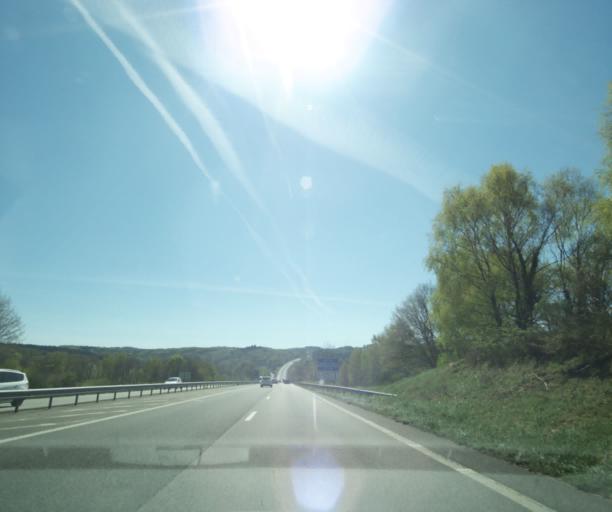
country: FR
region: Limousin
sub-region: Departement de la Haute-Vienne
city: Bessines-sur-Gartempe
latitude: 46.0800
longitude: 1.3568
